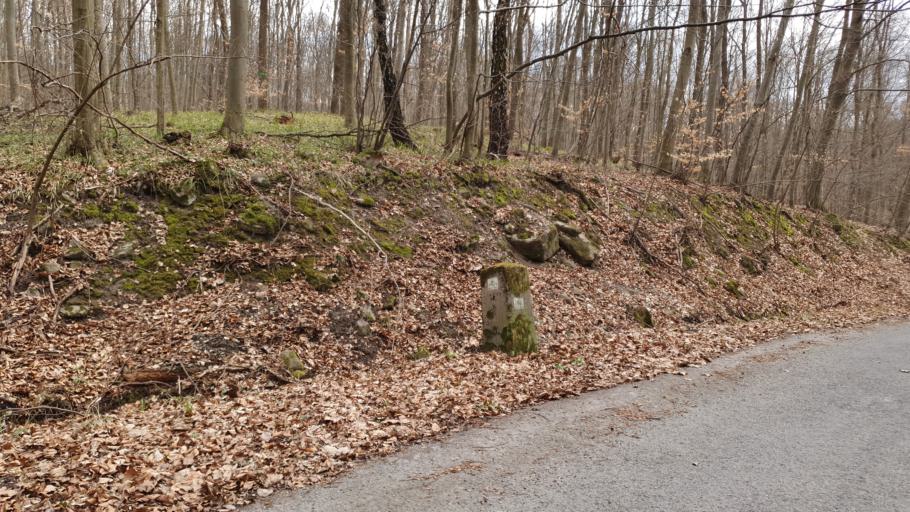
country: HU
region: Komarom-Esztergom
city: Pilismarot
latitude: 47.7450
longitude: 18.8580
